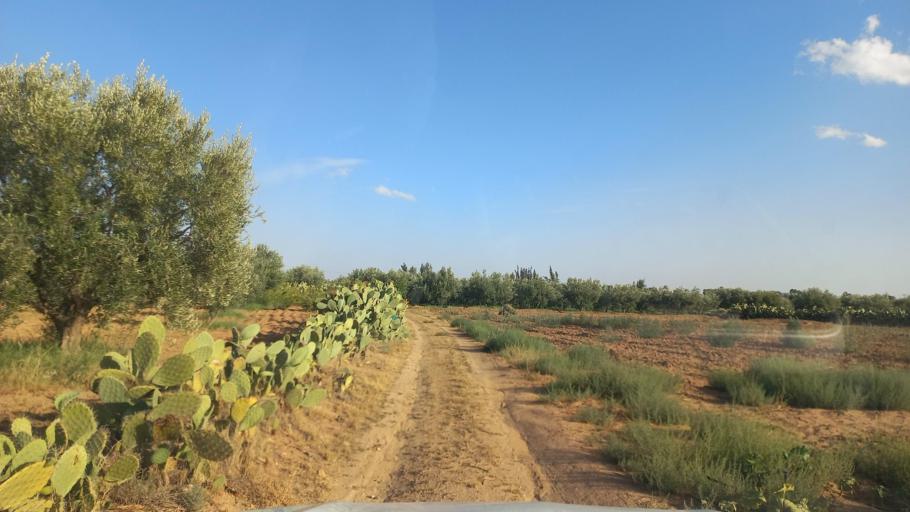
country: TN
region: Al Qasrayn
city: Kasserine
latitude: 35.2658
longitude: 9.0329
